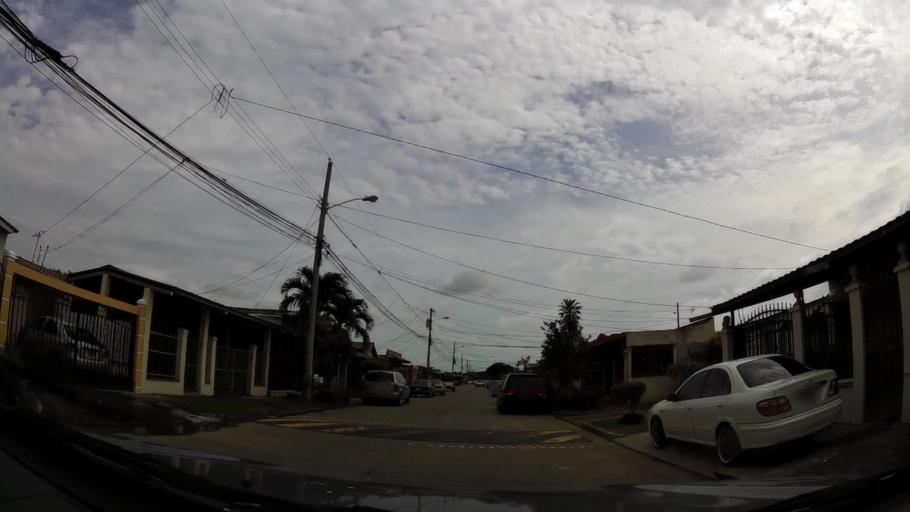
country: PA
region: Panama
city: Tocumen
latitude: 9.0446
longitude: -79.4115
